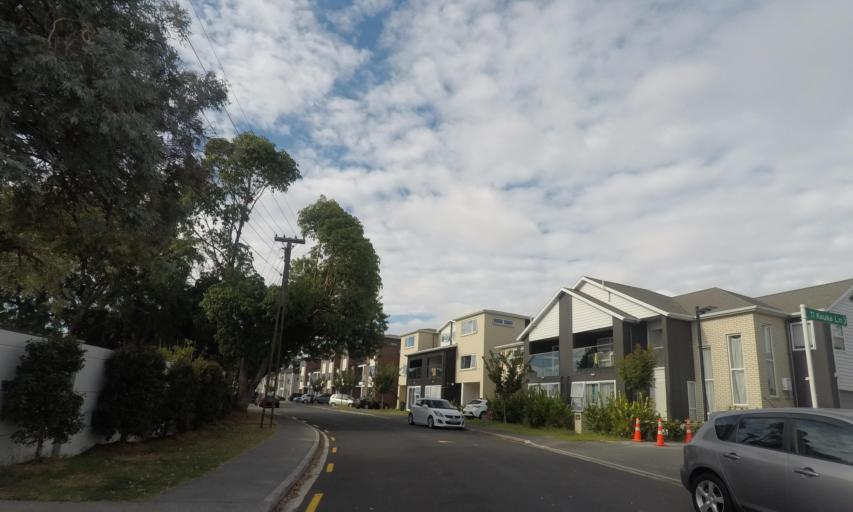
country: NZ
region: Auckland
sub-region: Auckland
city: Auckland
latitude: -36.8886
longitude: 174.7273
